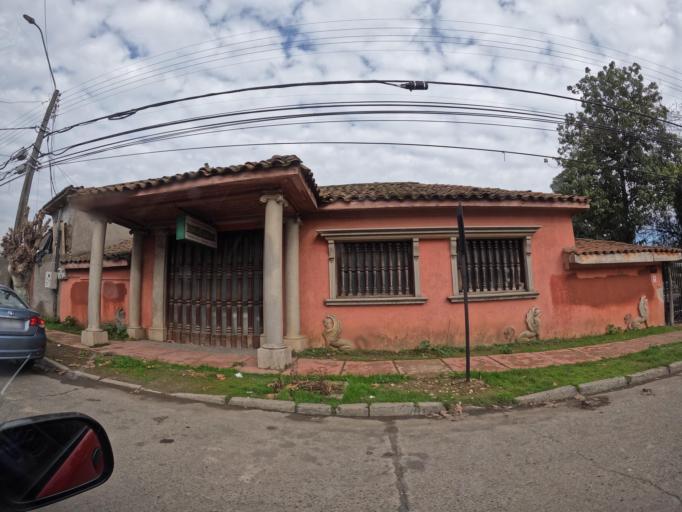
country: CL
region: Maule
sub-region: Provincia de Linares
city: Linares
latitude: -35.8425
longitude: -71.6029
